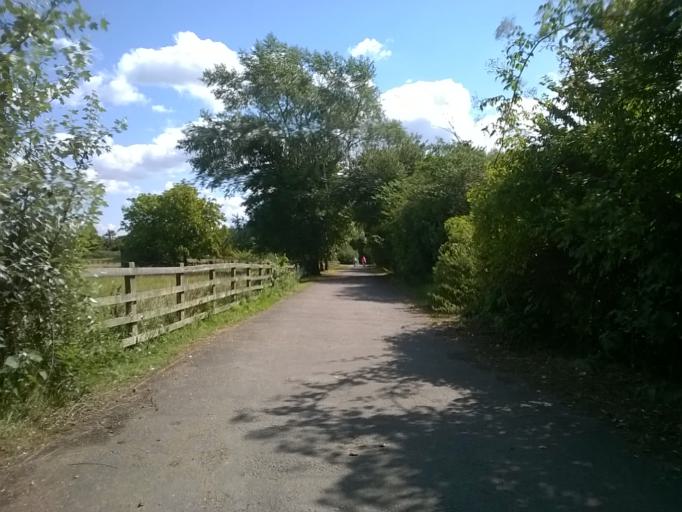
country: GB
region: England
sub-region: Milton Keynes
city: Milton Keynes
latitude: 52.0350
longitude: -0.7285
